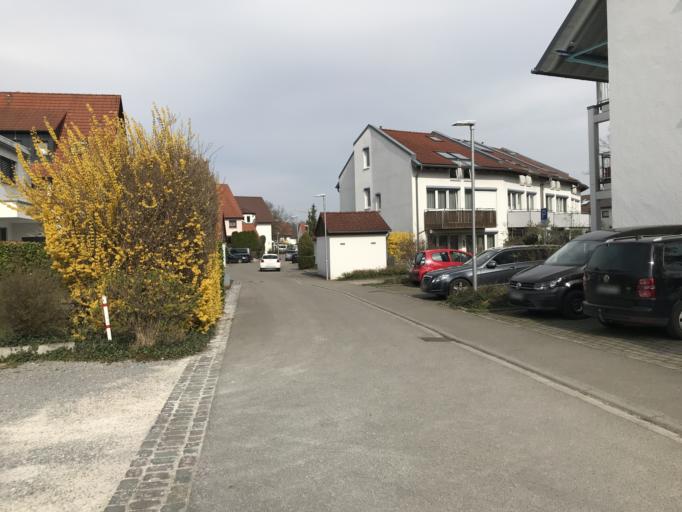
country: DE
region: Baden-Wuerttemberg
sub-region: Regierungsbezirk Stuttgart
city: Unterensingen
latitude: 48.6561
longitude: 9.3564
